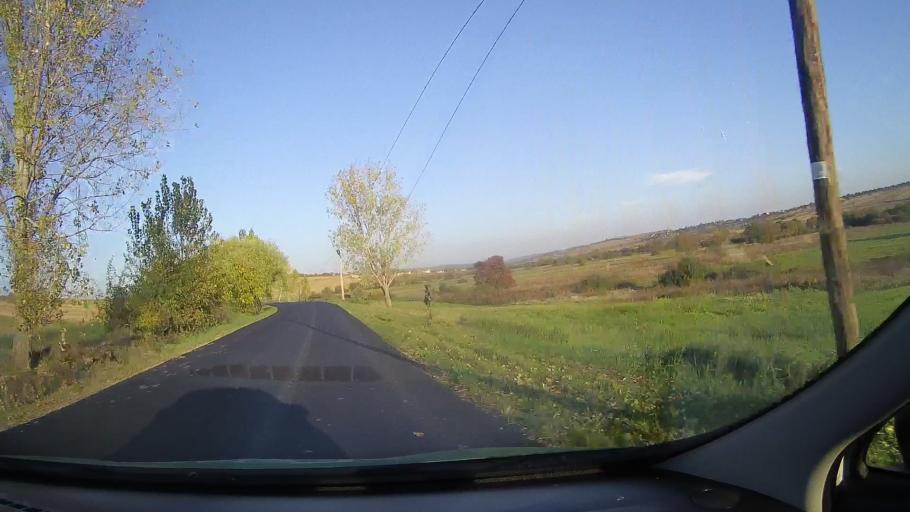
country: RO
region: Bihor
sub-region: Comuna Paleu
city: Paleu
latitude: 47.1297
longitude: 21.9776
